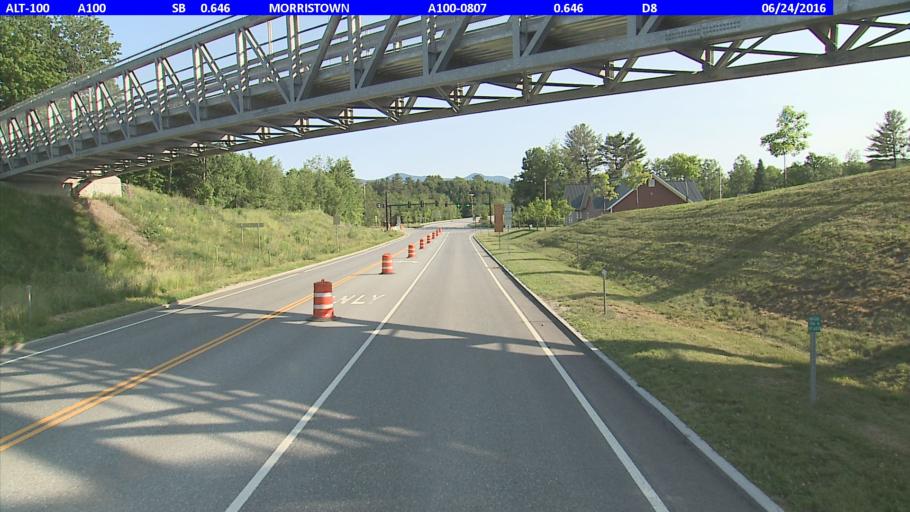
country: US
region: Vermont
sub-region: Lamoille County
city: Morrisville
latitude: 44.5653
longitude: -72.6039
